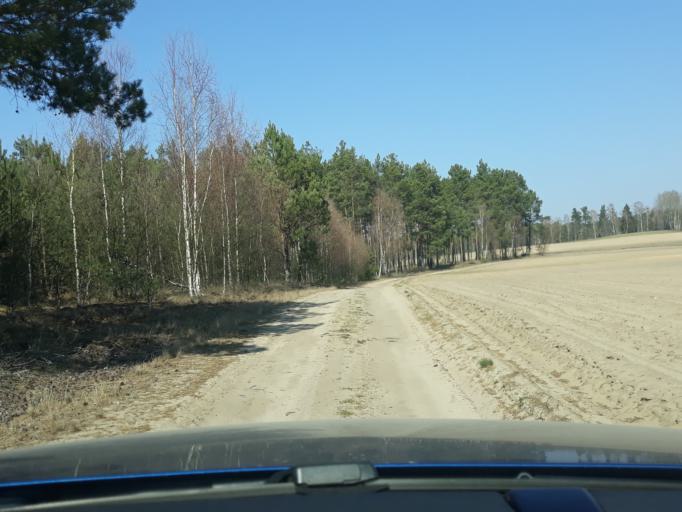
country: PL
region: Pomeranian Voivodeship
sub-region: Powiat bytowski
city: Lipnica
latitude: 53.8572
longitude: 17.4345
